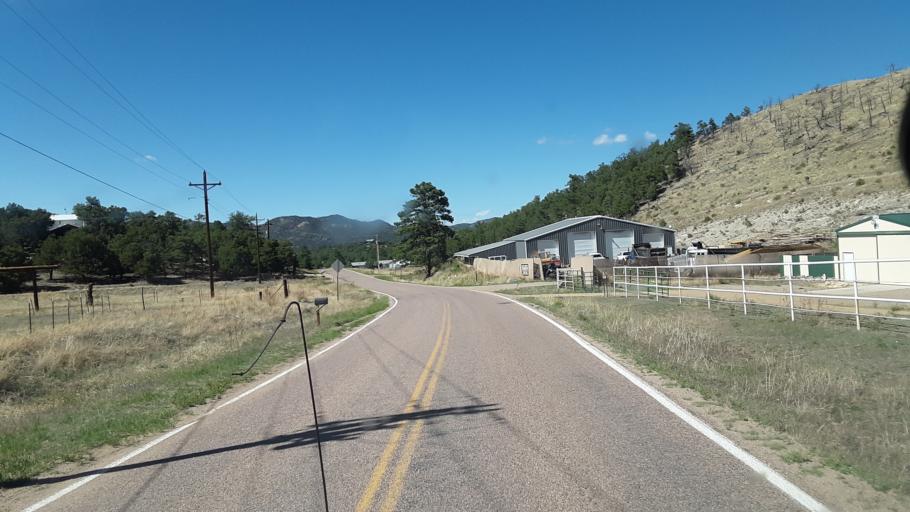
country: US
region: Colorado
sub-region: Custer County
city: Westcliffe
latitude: 38.3373
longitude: -105.4853
